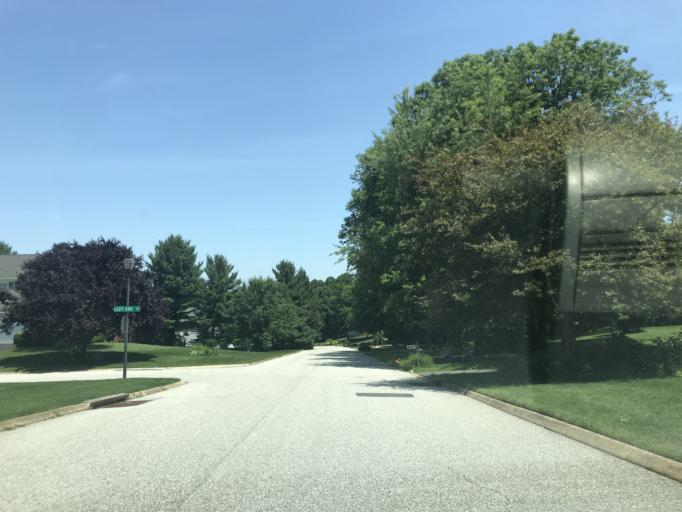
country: US
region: Maryland
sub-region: Harford County
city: South Bel Air
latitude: 39.5623
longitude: -76.2712
